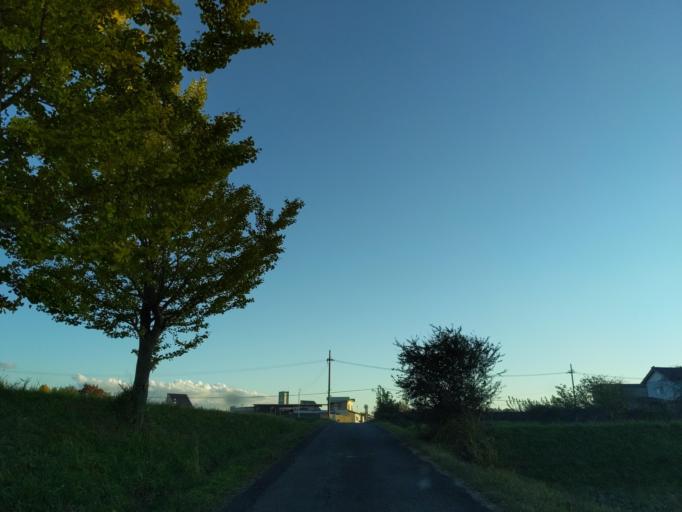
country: JP
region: Fukushima
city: Koriyama
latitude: 37.4450
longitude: 140.3735
